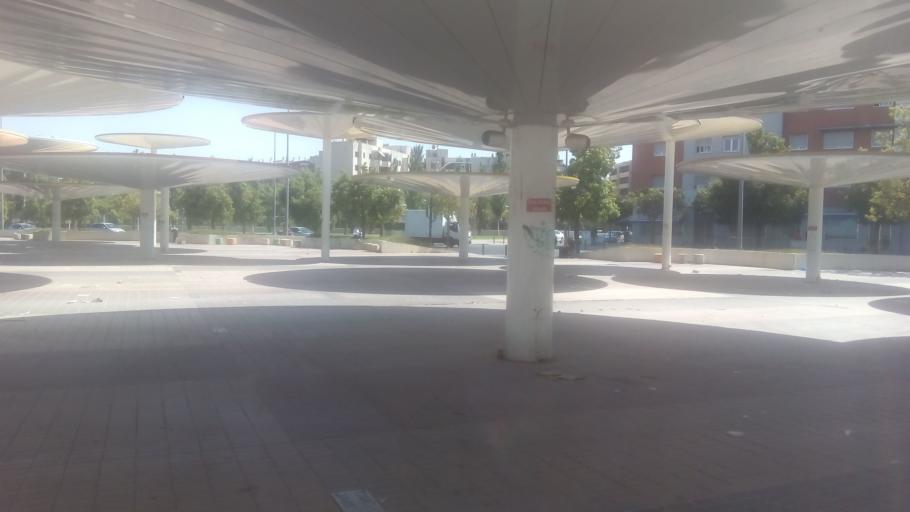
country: ES
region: Andalusia
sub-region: Province of Cordoba
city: Cordoba
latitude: 37.8861
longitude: -4.7982
